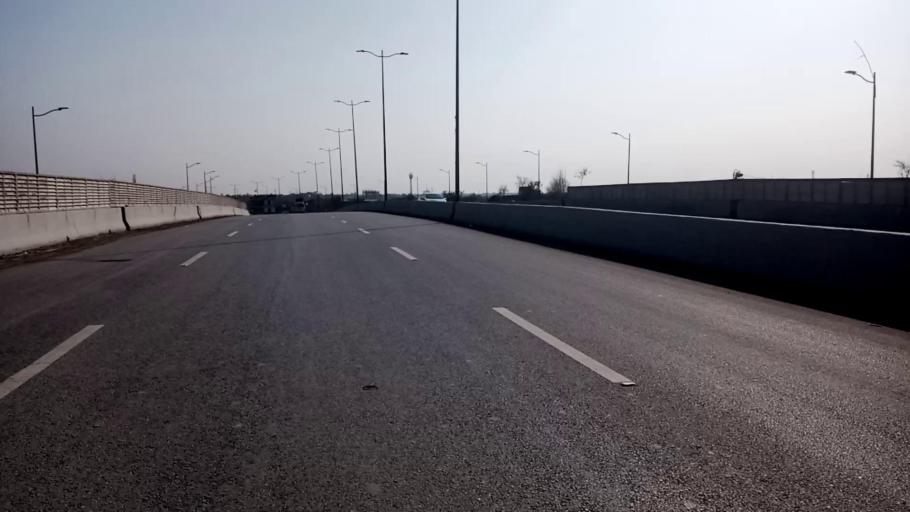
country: PK
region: Khyber Pakhtunkhwa
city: Peshawar
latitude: 34.0366
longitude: 71.5408
